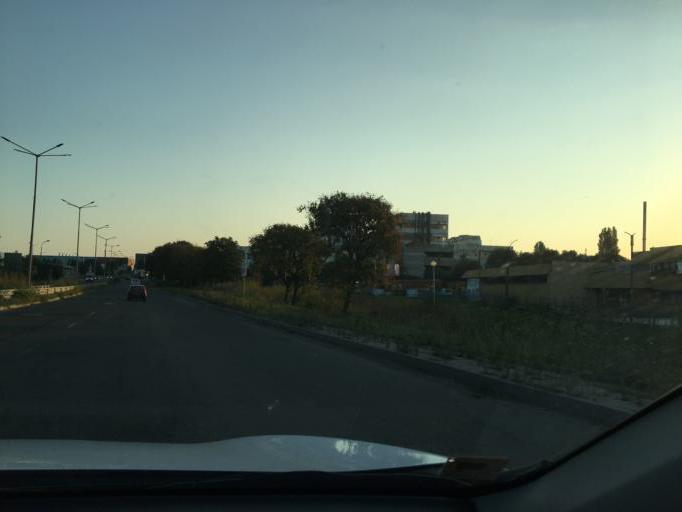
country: BG
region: Burgas
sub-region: Obshtina Burgas
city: Burgas
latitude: 42.5175
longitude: 27.4376
